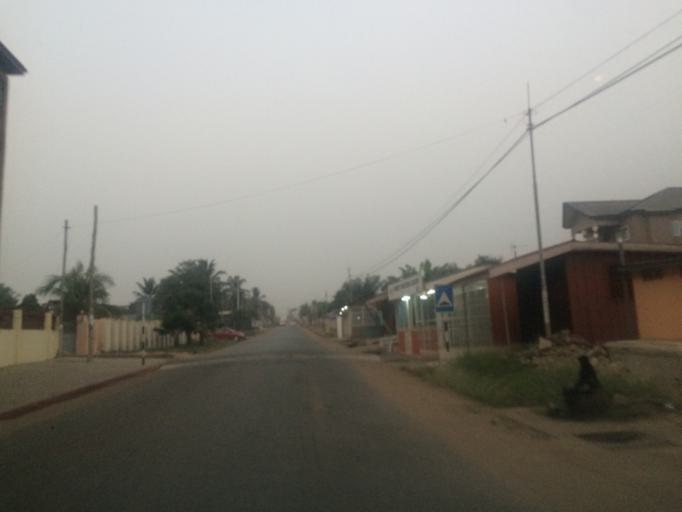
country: GH
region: Greater Accra
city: Teshi Old Town
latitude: 5.5986
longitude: -0.0994
